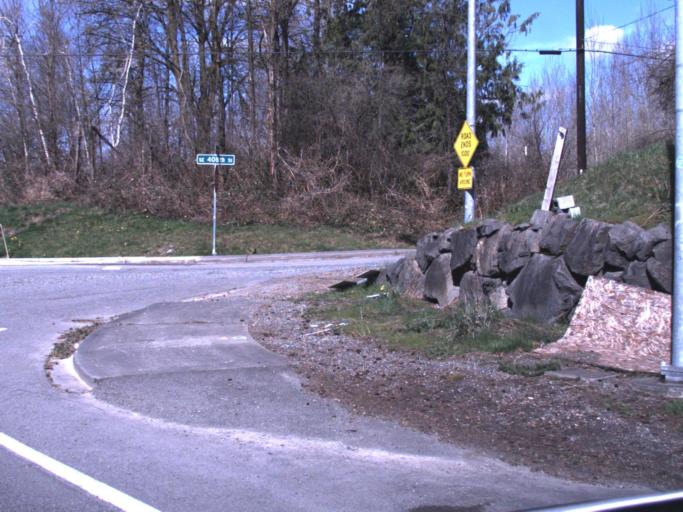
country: US
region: Washington
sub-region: King County
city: Lake Morton-Berrydale
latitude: 47.2356
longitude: -122.1070
